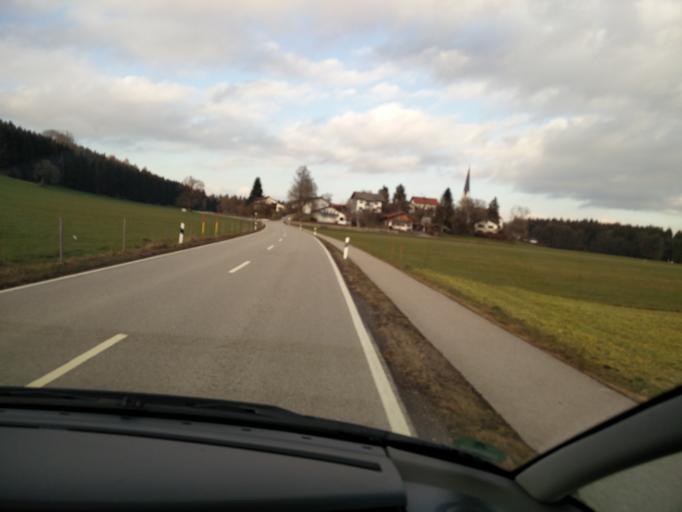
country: DE
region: Bavaria
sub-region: Upper Bavaria
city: Rimsting
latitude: 47.9162
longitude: 12.3385
